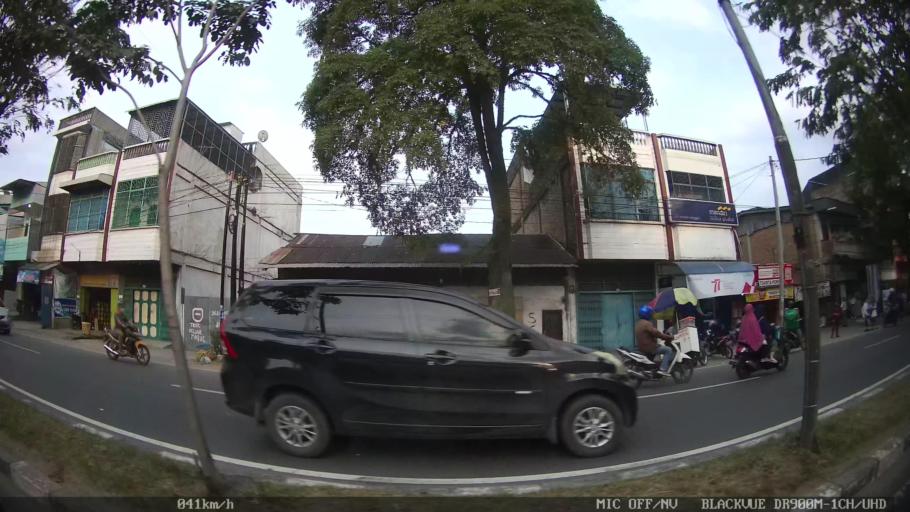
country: ID
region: North Sumatra
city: Sunggal
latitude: 3.5738
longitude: 98.6109
